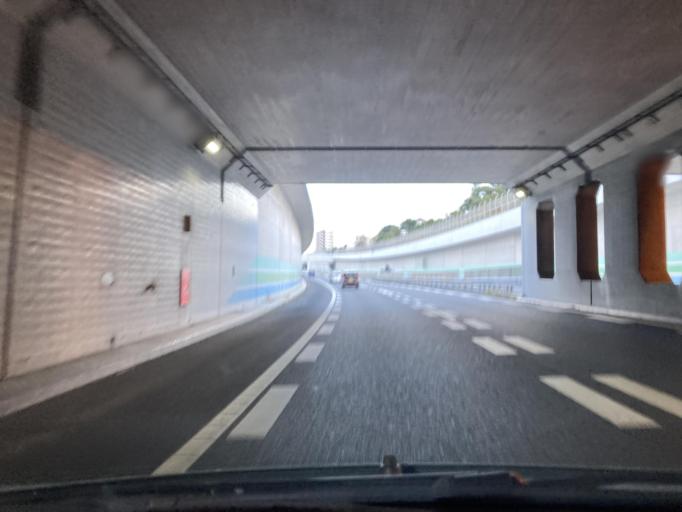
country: JP
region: Okinawa
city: Okinawa
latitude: 26.3304
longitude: 127.7844
